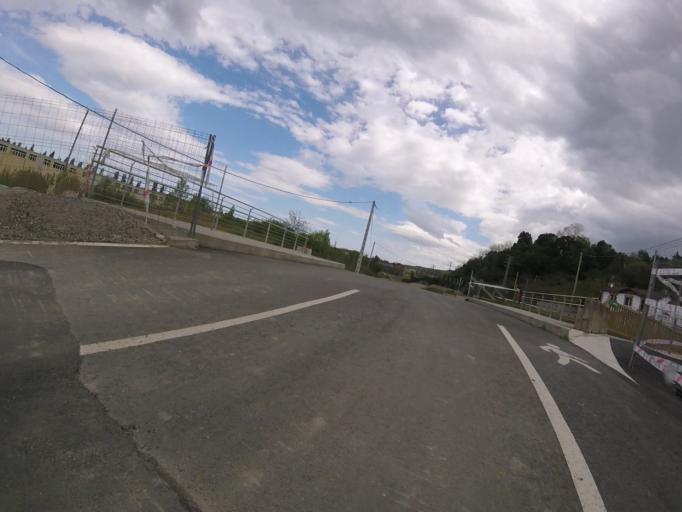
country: ES
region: Basque Country
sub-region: Provincia de Guipuzcoa
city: Zarautz
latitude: 43.2763
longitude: -2.1702
